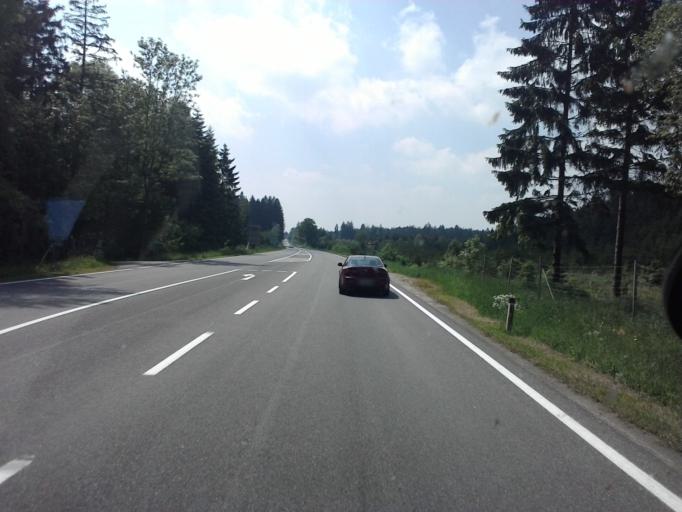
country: AT
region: Upper Austria
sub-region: Politischer Bezirk Steyr-Land
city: Sierning
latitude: 48.0350
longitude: 14.2914
